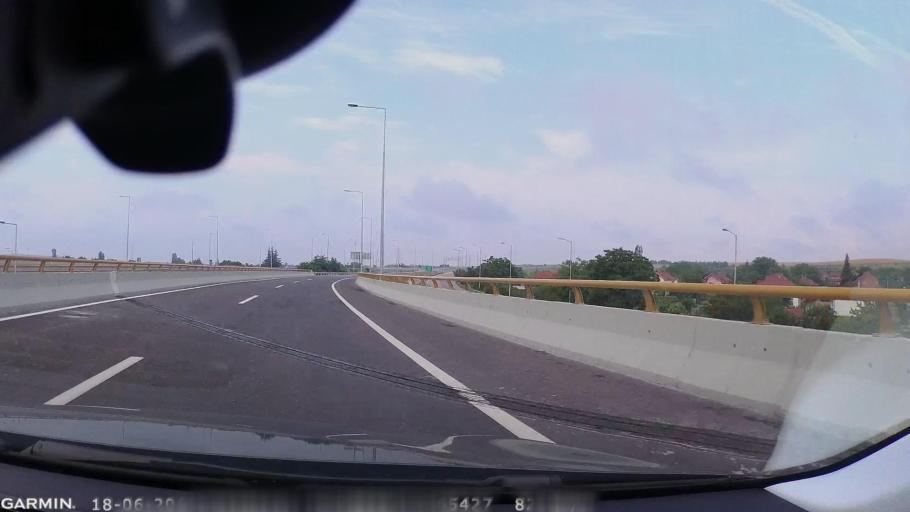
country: MK
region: Petrovec
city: Sredno Konjare
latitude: 41.9512
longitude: 21.7595
